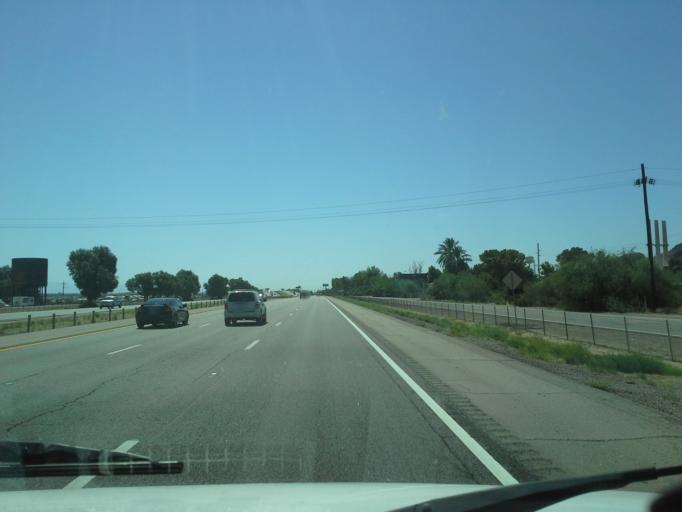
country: US
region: Arizona
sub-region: Pima County
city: Marana
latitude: 32.4159
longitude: -111.1525
